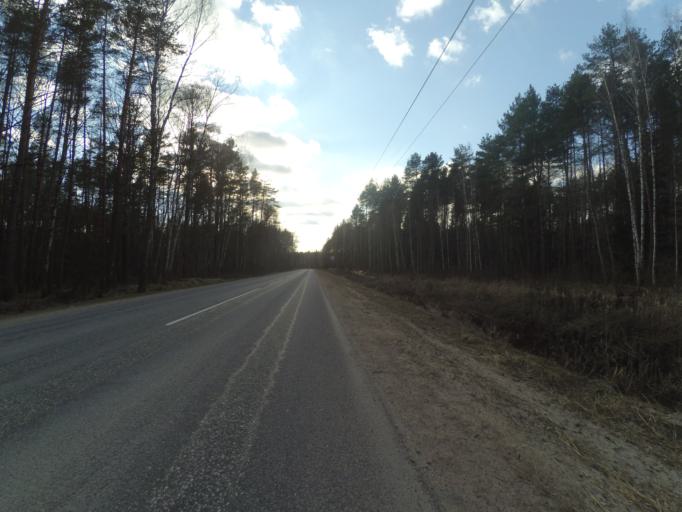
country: RU
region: Moskovskaya
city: Pushchino
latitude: 54.9044
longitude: 37.6790
